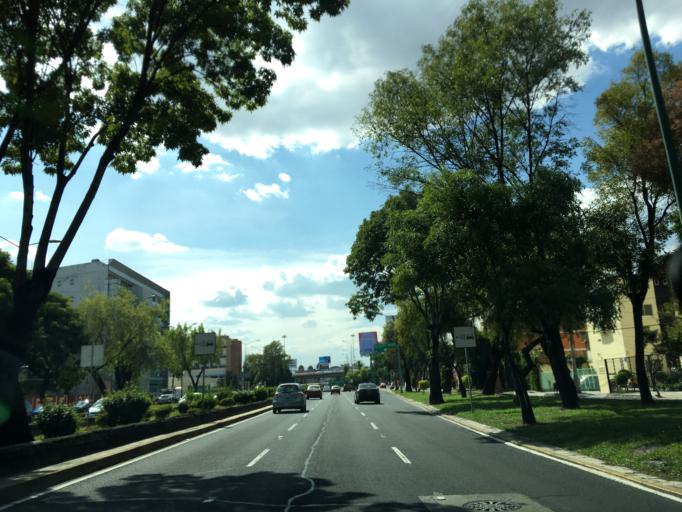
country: MX
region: Mexico City
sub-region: Iztacalco
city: Iztacalco
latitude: 19.4067
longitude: -99.1103
